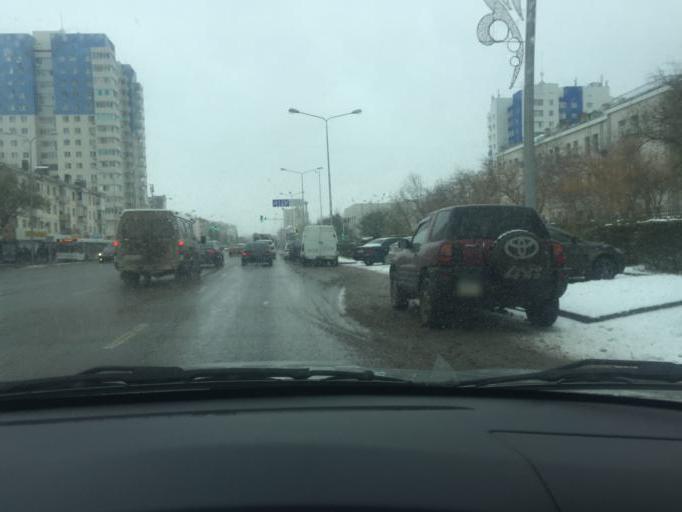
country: KZ
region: Astana Qalasy
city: Astana
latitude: 51.1841
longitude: 71.4089
